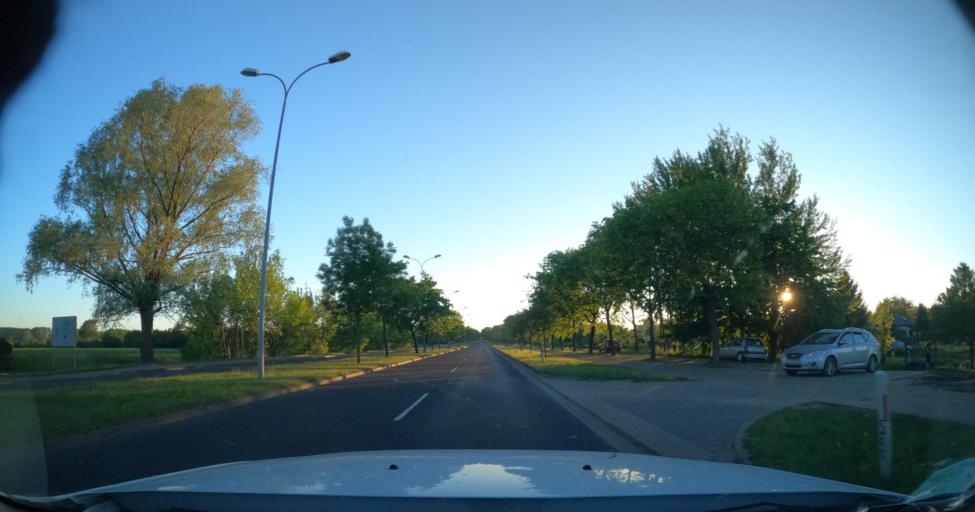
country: PL
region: Pomeranian Voivodeship
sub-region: Slupsk
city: Slupsk
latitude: 54.4700
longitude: 17.0730
